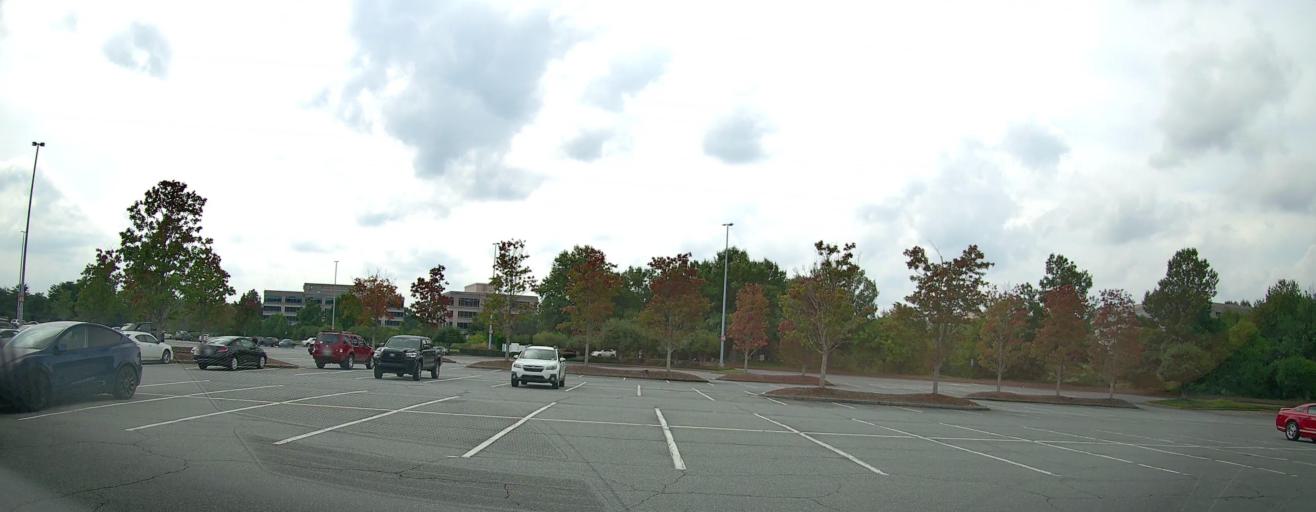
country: US
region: Georgia
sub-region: Fulton County
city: Alpharetta
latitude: 34.0486
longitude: -84.2975
